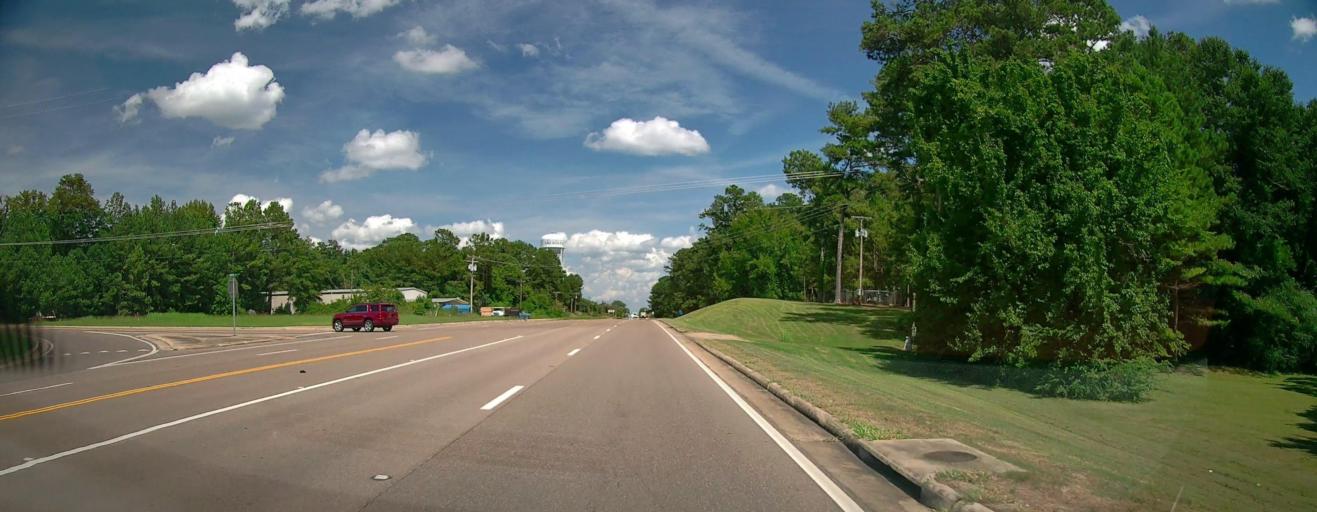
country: US
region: Mississippi
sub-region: Monroe County
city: Aberdeen
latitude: 33.8148
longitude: -88.5622
